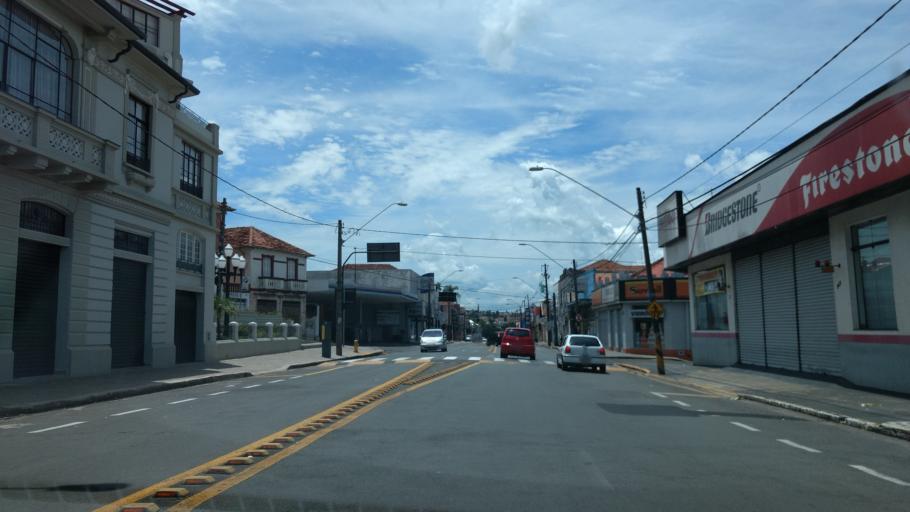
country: BR
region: Sao Paulo
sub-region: Botucatu
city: Botucatu
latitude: -22.8822
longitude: -48.4410
